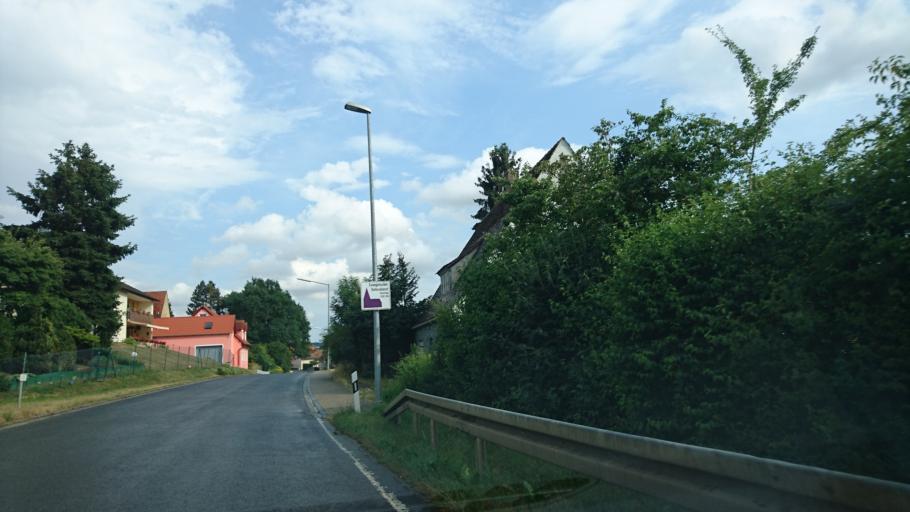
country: DE
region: Bavaria
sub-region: Regierungsbezirk Mittelfranken
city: Thalmassing
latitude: 49.1101
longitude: 11.1817
